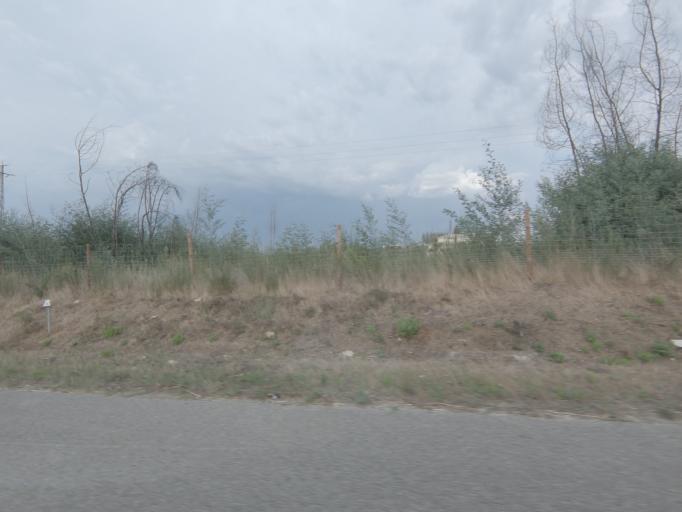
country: PT
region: Viseu
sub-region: Concelho de Tondela
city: Tondela
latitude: 40.5047
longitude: -8.0843
